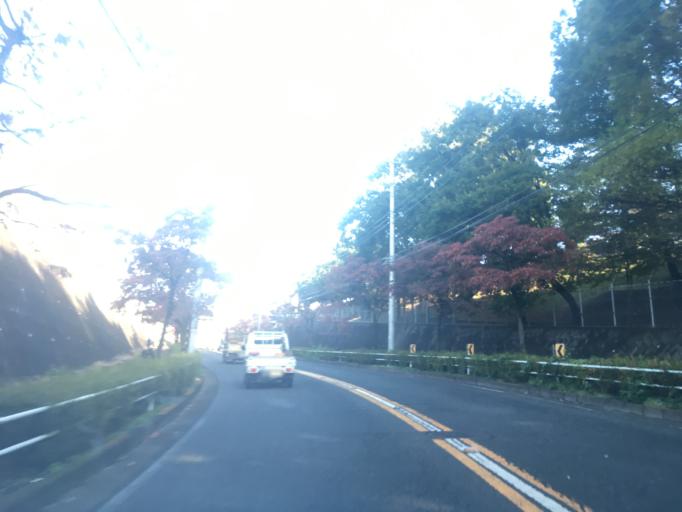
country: JP
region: Tokyo
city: Hino
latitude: 35.6833
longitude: 139.3587
